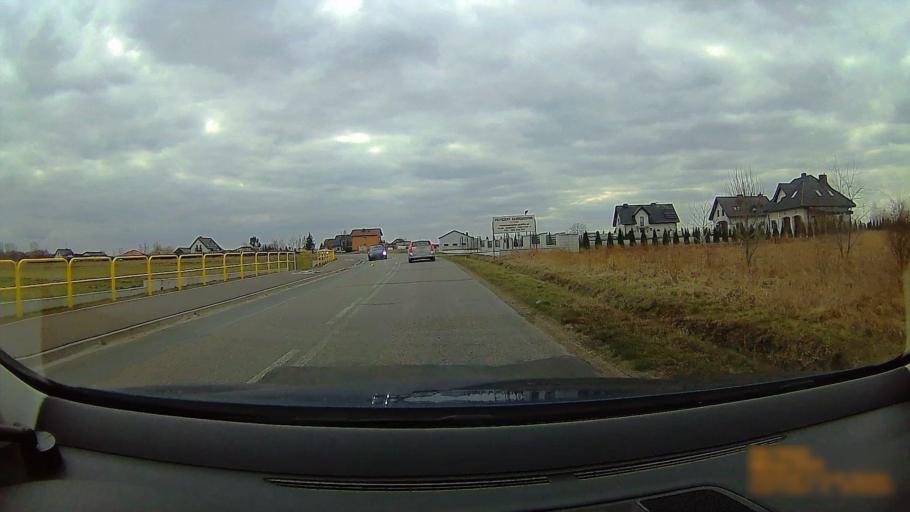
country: PL
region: Greater Poland Voivodeship
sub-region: Powiat koninski
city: Golina
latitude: 52.1918
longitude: 18.1192
